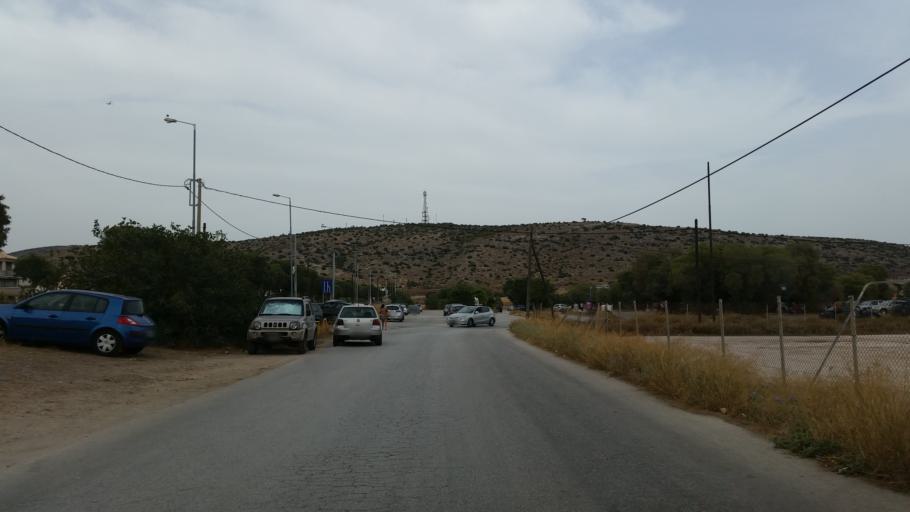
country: GR
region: Attica
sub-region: Nomarchia Anatolikis Attikis
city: Vari
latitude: 37.8218
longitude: 23.8092
